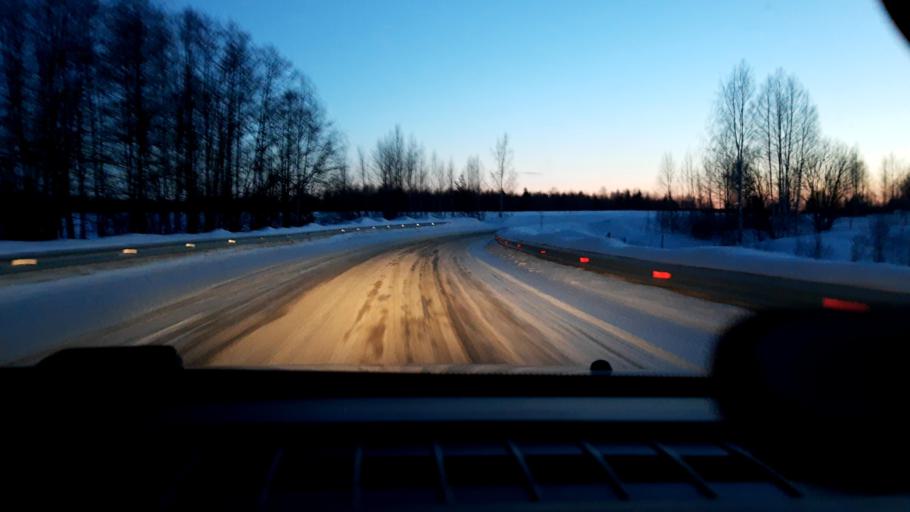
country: RU
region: Nizjnij Novgorod
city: Spasskoye
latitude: 56.1544
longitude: 45.4415
